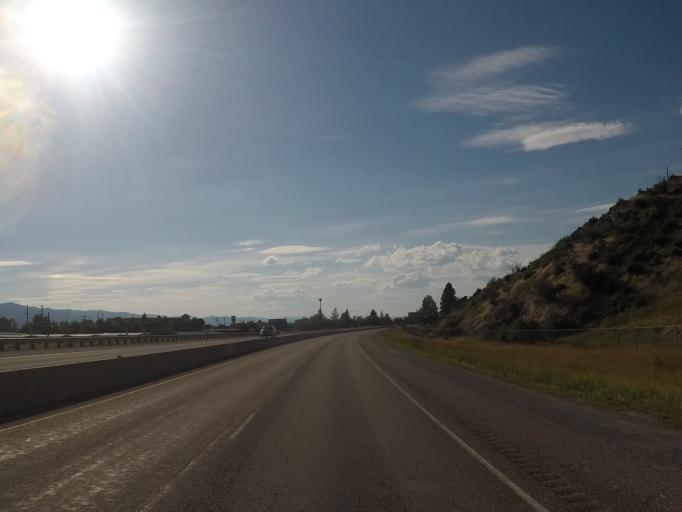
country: US
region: Montana
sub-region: Missoula County
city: Missoula
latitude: 46.8660
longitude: -113.9732
